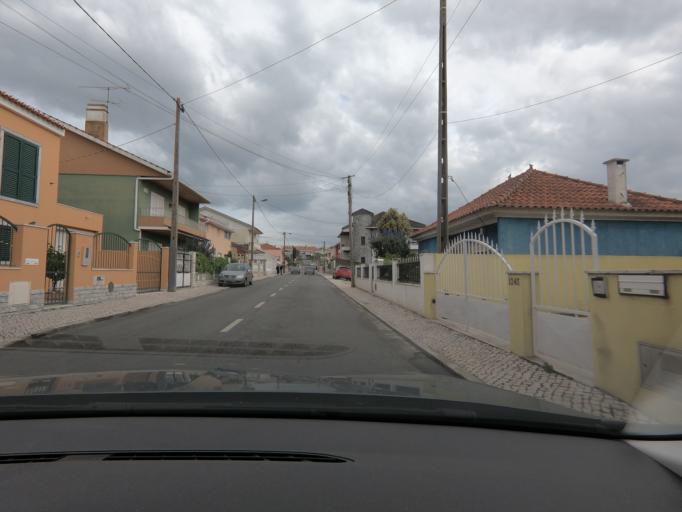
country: PT
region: Lisbon
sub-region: Cascais
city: Sao Domingos de Rana
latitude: 38.7215
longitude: -9.3327
